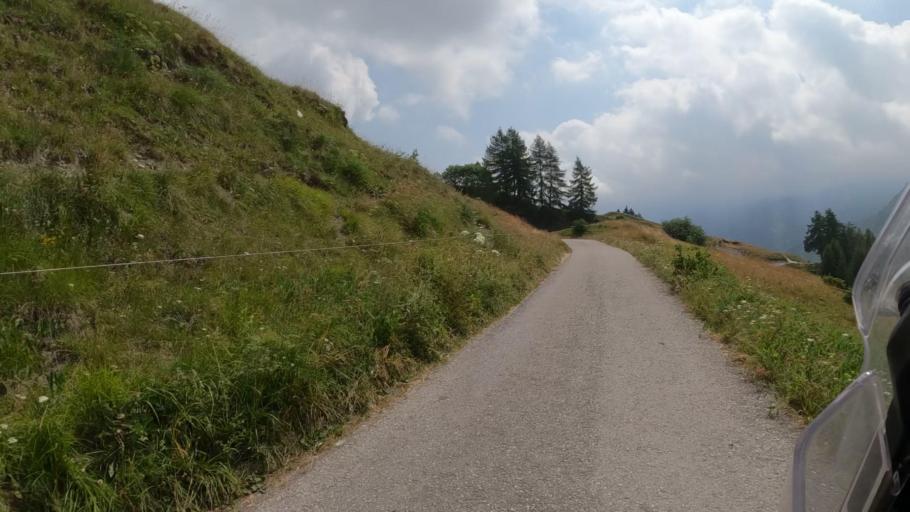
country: IT
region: Piedmont
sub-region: Provincia di Cuneo
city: Campomolino
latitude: 44.4021
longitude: 7.1651
